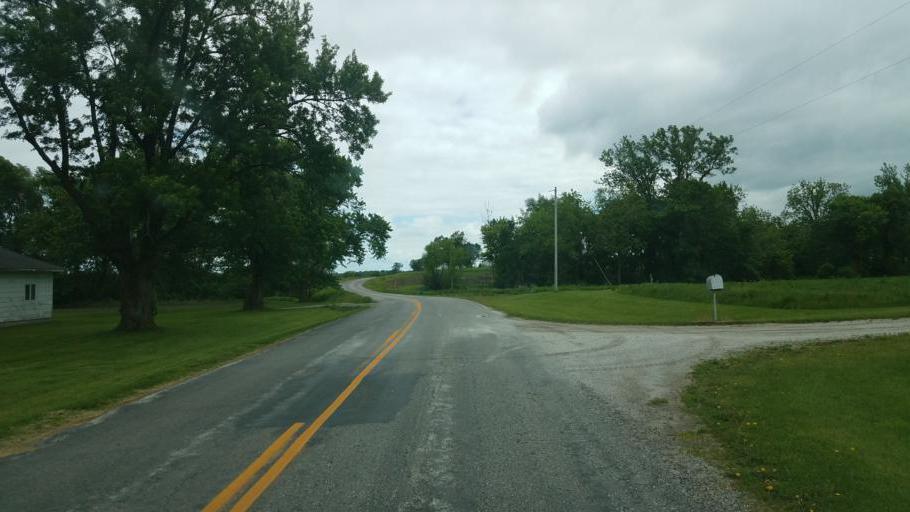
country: US
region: Iowa
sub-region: Decatur County
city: Lamoni
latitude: 40.4731
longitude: -93.8222
